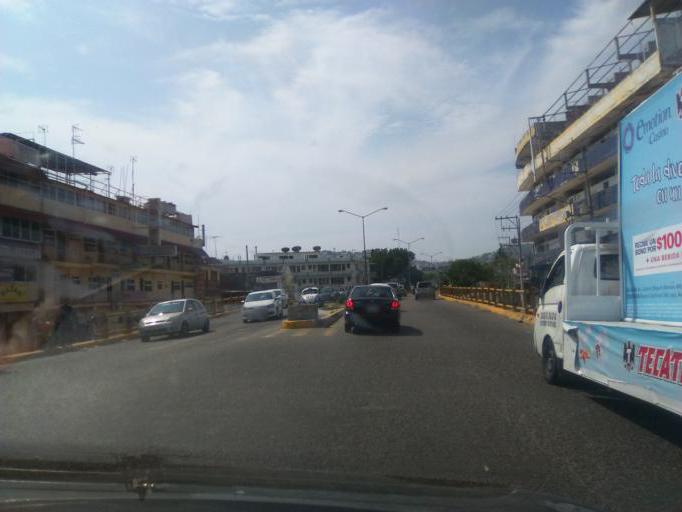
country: MX
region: Guerrero
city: Acapulco de Juarez
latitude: 16.8578
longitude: -99.9039
